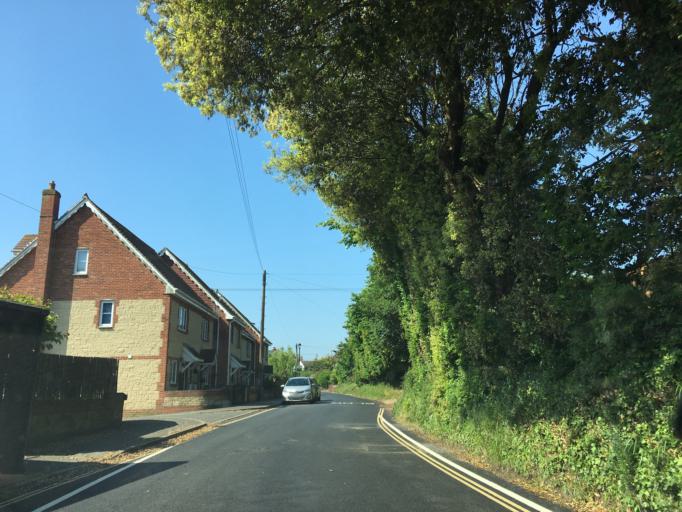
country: GB
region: England
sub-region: Isle of Wight
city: Newchurch
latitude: 50.6647
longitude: -1.2080
